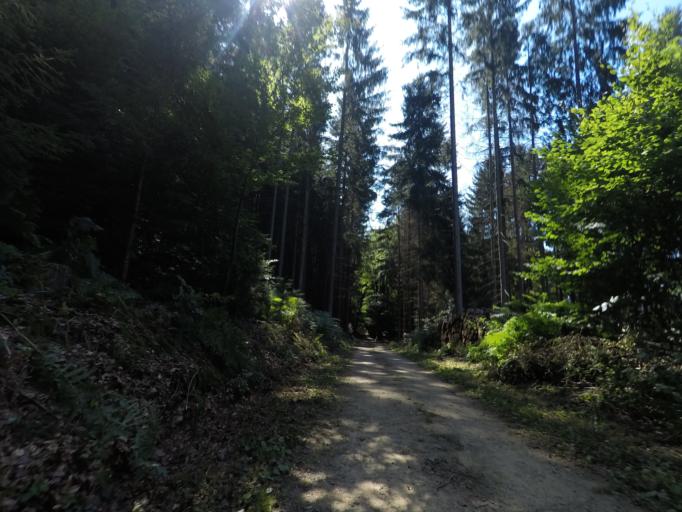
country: LU
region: Luxembourg
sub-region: Canton de Capellen
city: Kopstal
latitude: 49.6496
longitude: 6.0591
